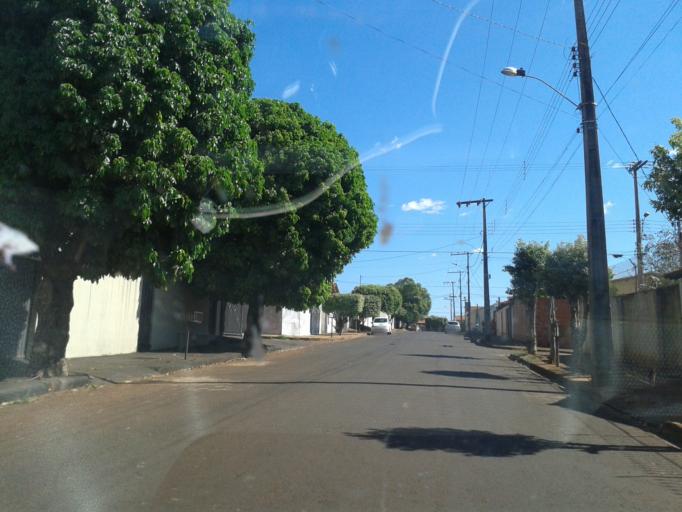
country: BR
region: Minas Gerais
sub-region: Ituiutaba
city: Ituiutaba
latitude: -18.9518
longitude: -49.4614
